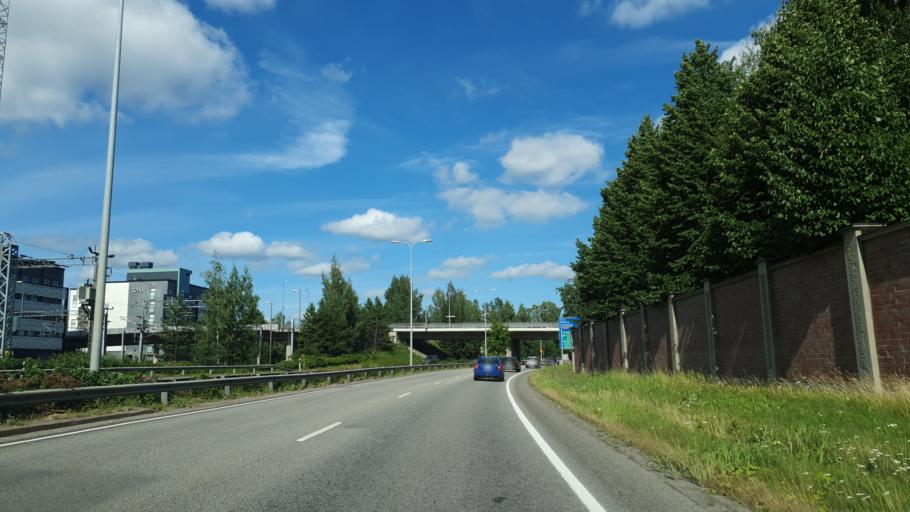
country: FI
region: Central Finland
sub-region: Jyvaeskylae
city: Jyvaeskylae
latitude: 62.2433
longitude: 25.7603
